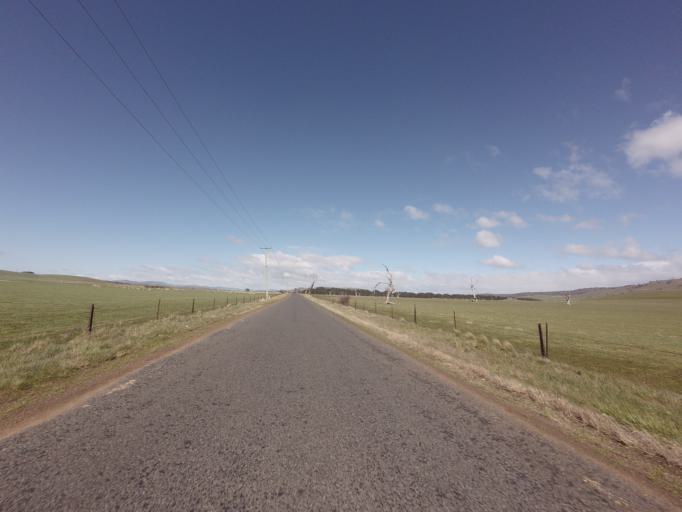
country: AU
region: Tasmania
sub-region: Northern Midlands
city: Evandale
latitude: -41.9890
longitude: 147.4518
